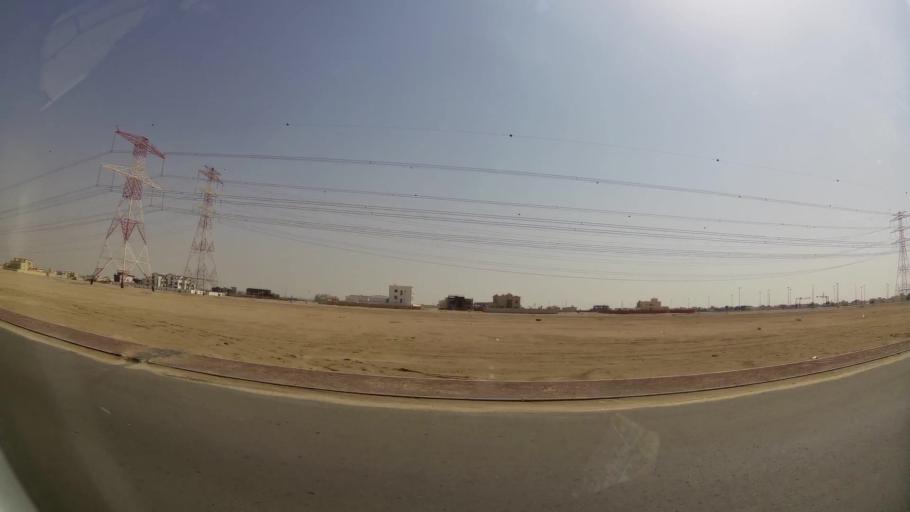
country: AE
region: Abu Dhabi
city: Abu Dhabi
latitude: 24.3063
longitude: 54.5679
